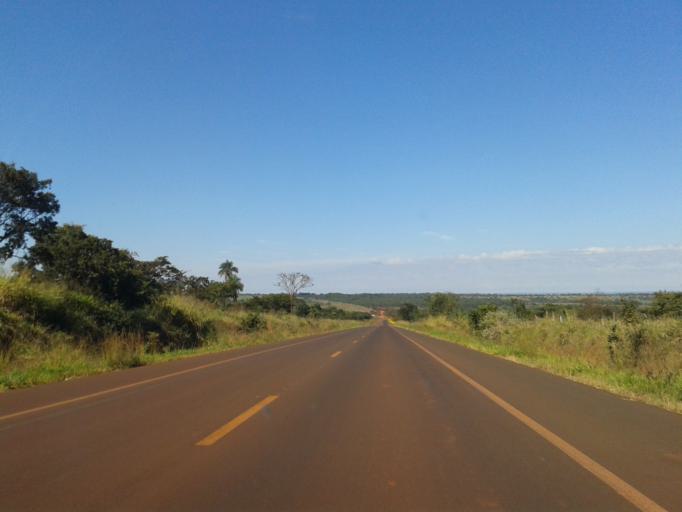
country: BR
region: Minas Gerais
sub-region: Ituiutaba
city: Ituiutaba
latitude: -19.0356
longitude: -49.5037
